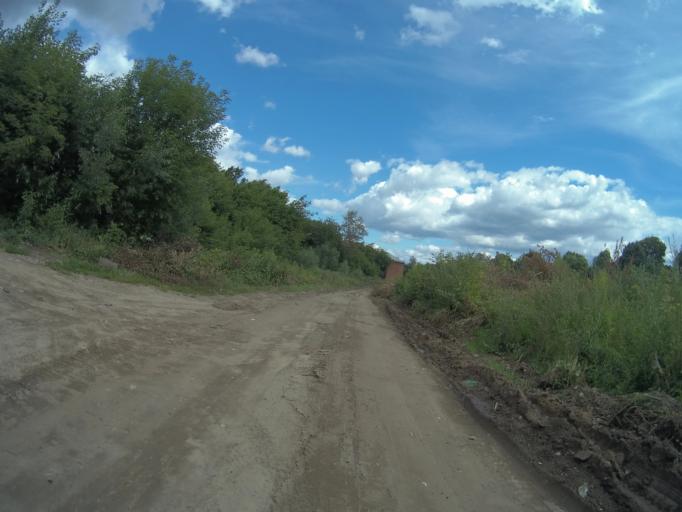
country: RU
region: Vladimir
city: Vladimir
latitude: 56.1350
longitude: 40.4114
